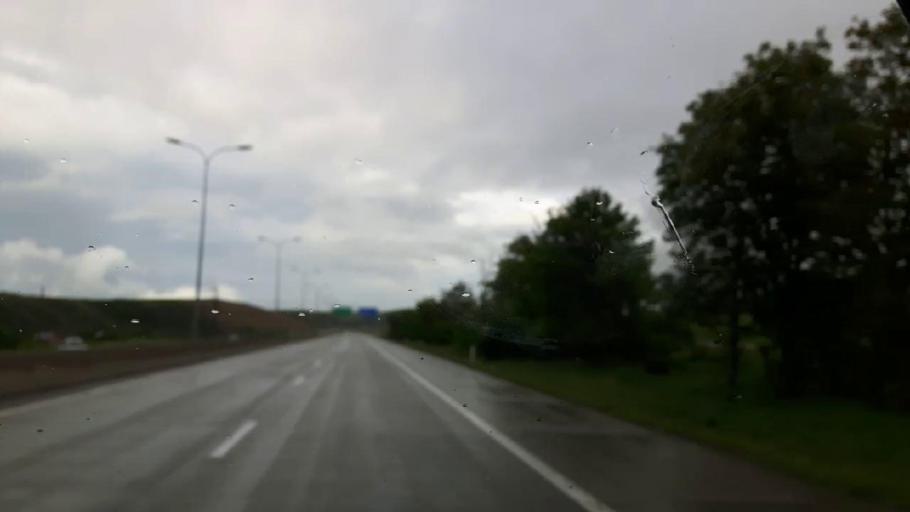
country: GE
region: Shida Kartli
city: Kaspi
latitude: 42.0004
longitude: 44.3863
